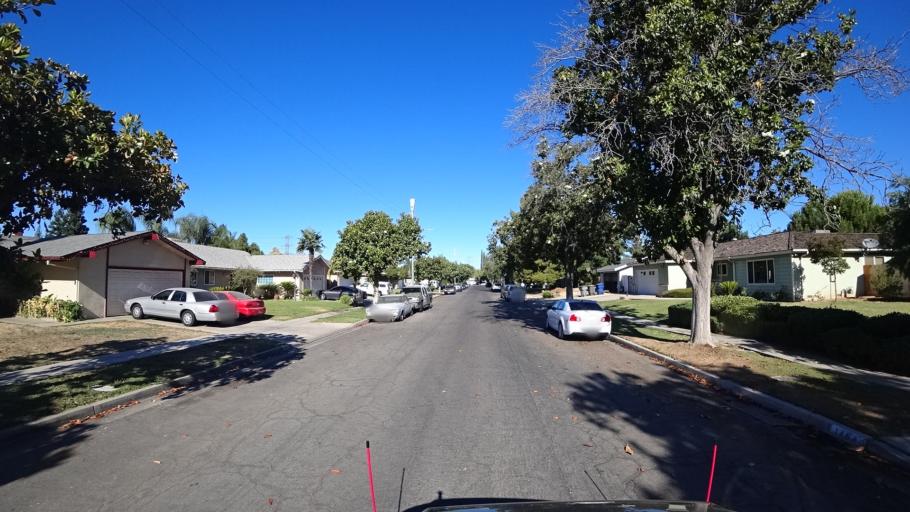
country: US
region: California
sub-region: Fresno County
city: Fresno
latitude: 36.7973
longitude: -119.8282
